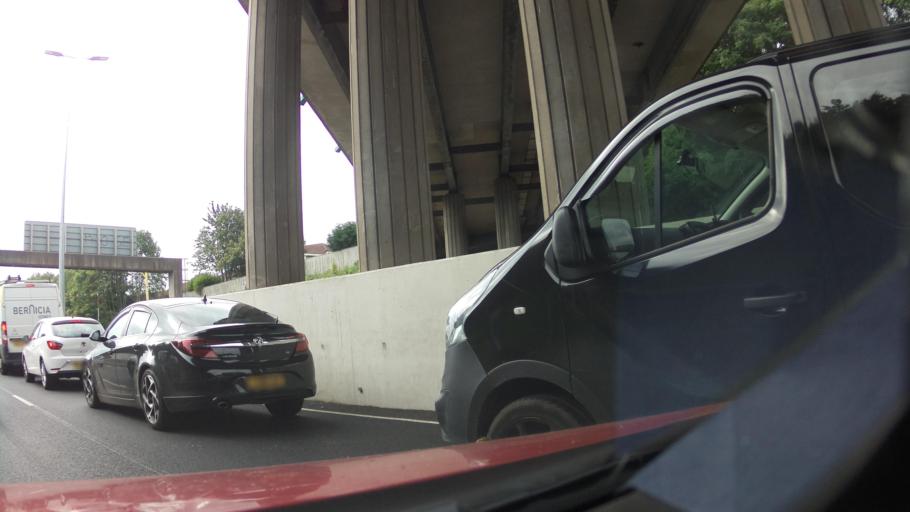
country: GB
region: England
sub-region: Newcastle upon Tyne
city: Benwell
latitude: 55.0017
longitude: -1.6731
